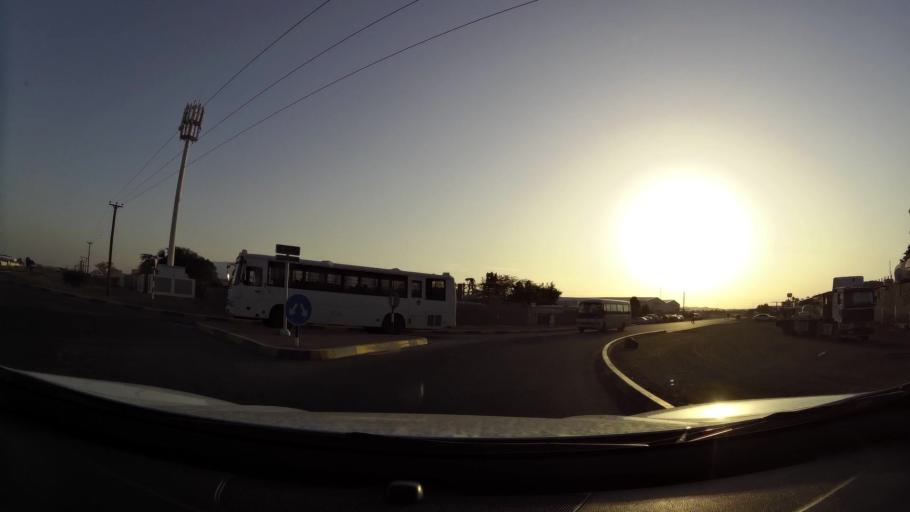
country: AE
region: Abu Dhabi
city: Al Ain
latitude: 24.1451
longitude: 55.8197
